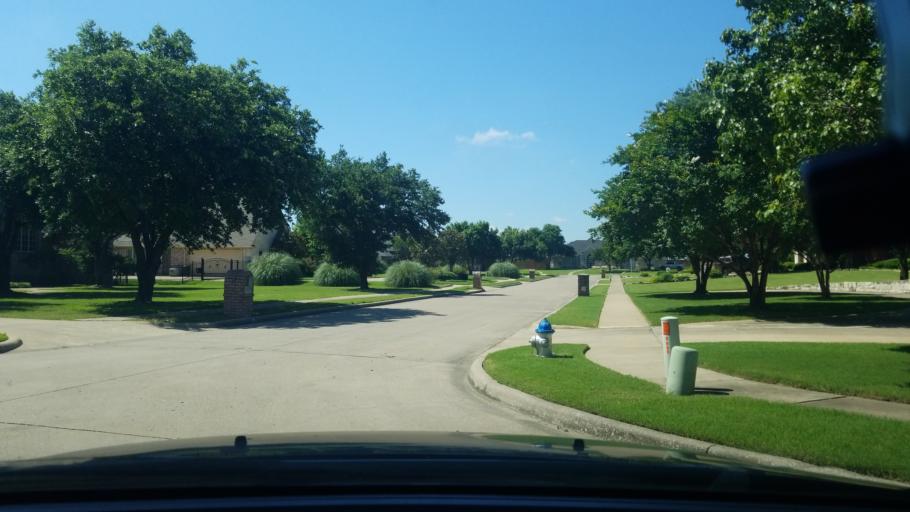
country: US
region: Texas
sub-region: Dallas County
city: Sunnyvale
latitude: 32.7910
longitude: -96.5764
